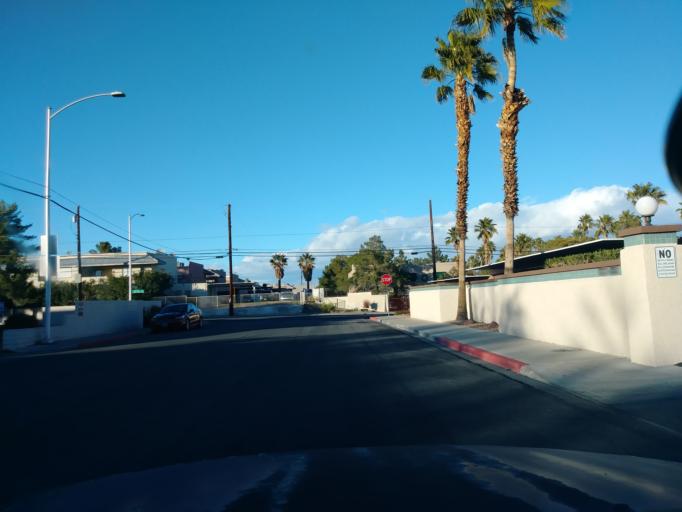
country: US
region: Nevada
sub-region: Clark County
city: Spring Valley
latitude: 36.1549
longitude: -115.2412
